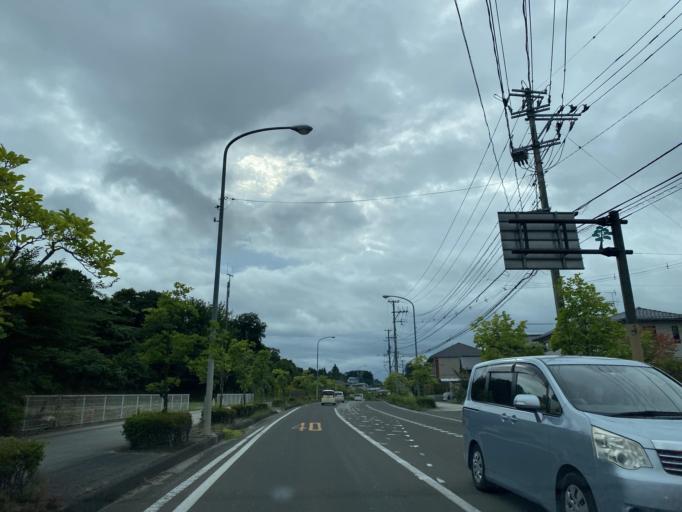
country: JP
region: Miyagi
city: Tomiya
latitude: 38.3956
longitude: 140.8967
